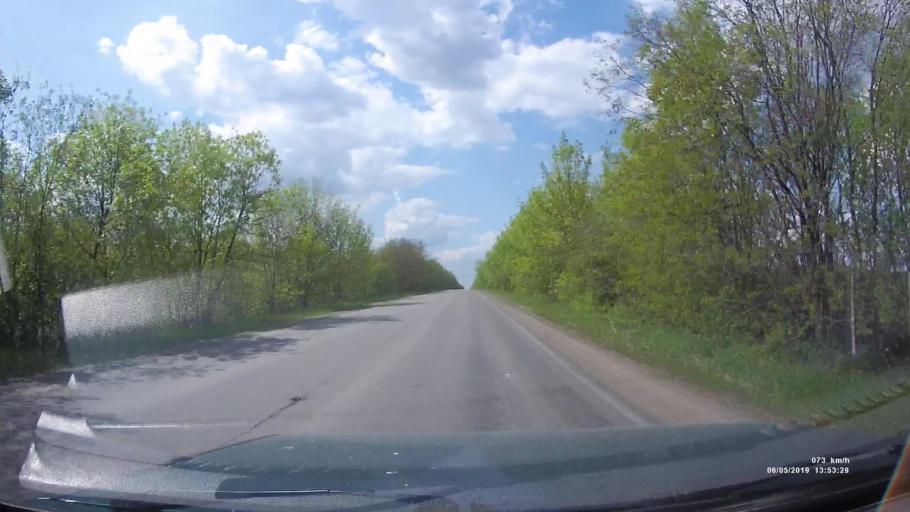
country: RU
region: Rostov
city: Melikhovskaya
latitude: 47.6685
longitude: 40.4619
